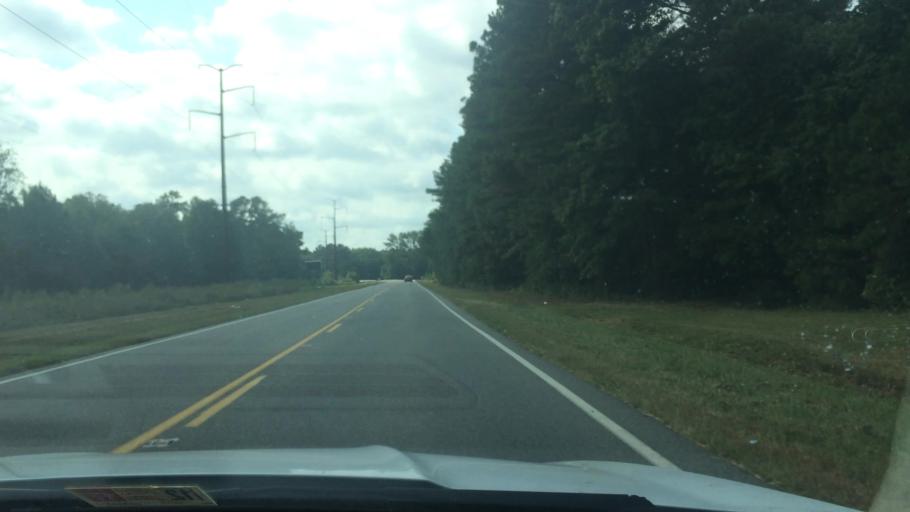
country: US
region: Virginia
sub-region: Middlesex County
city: Deltaville
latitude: 37.5939
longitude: -76.4610
